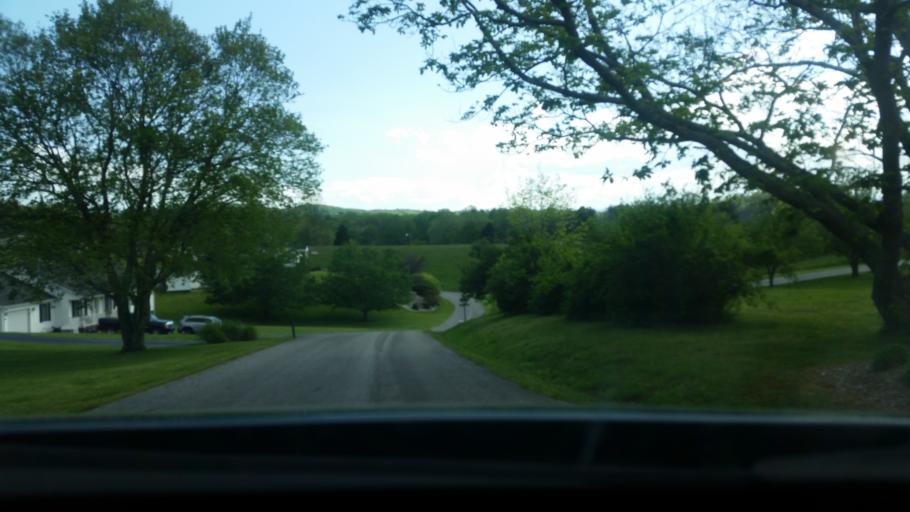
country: US
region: Virginia
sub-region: Giles County
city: Pembroke
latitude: 37.3171
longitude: -80.6299
